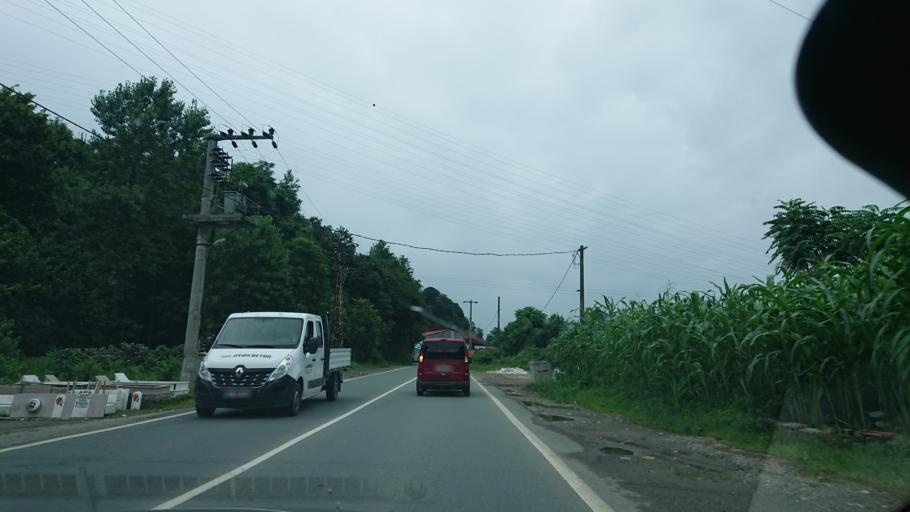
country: TR
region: Rize
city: Gundogdu
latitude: 41.0326
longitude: 40.5818
